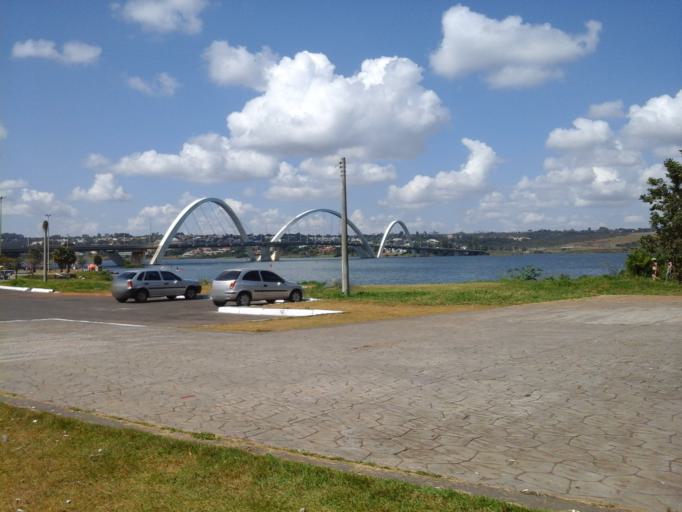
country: BR
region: Federal District
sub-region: Brasilia
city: Brasilia
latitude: -15.8197
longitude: -47.8355
